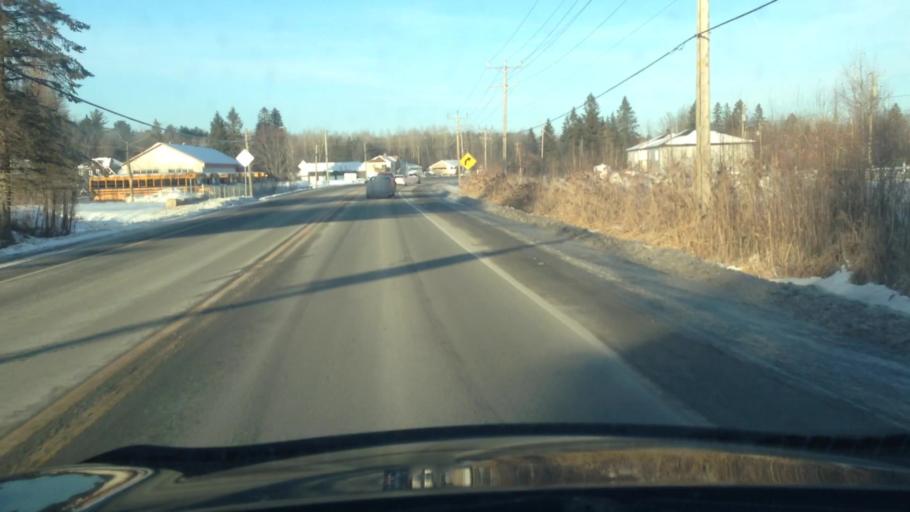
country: CA
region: Quebec
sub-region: Laurentides
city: Sainte-Sophie
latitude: 45.8274
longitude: -73.8861
